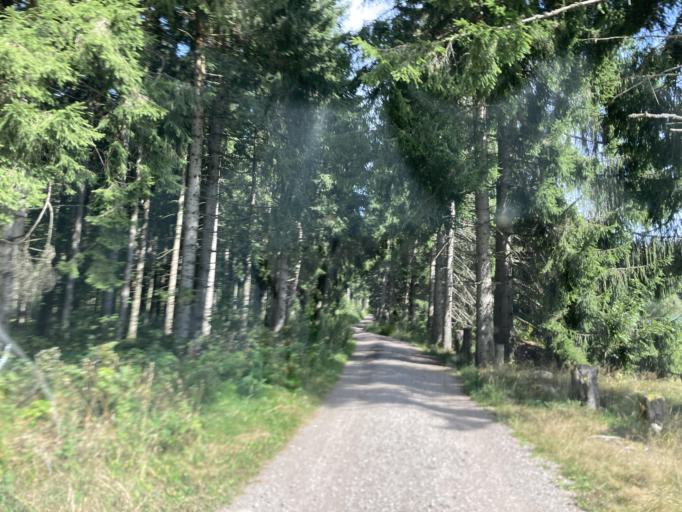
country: DE
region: Baden-Wuerttemberg
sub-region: Freiburg Region
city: Triberg im Schwarzwald
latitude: 48.0873
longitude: 8.2481
